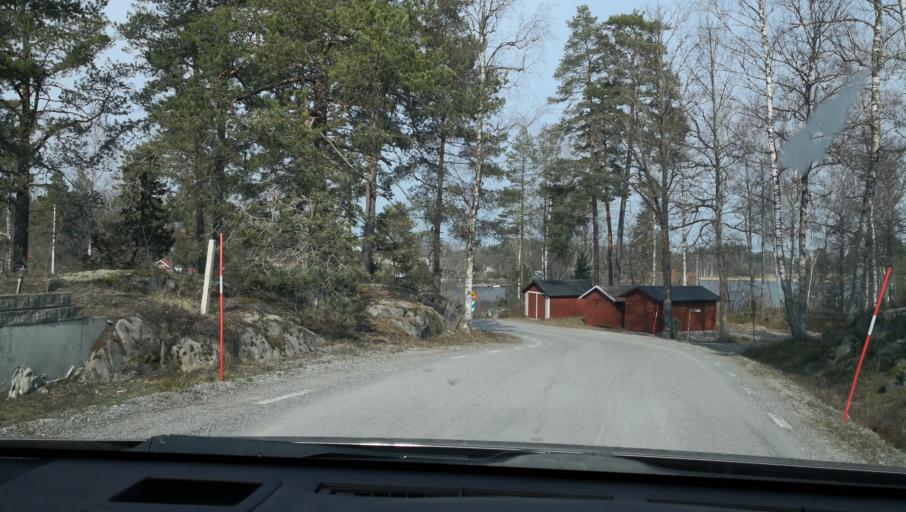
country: SE
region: OErebro
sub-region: Lindesbergs Kommun
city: Frovi
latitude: 59.3907
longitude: 15.3938
